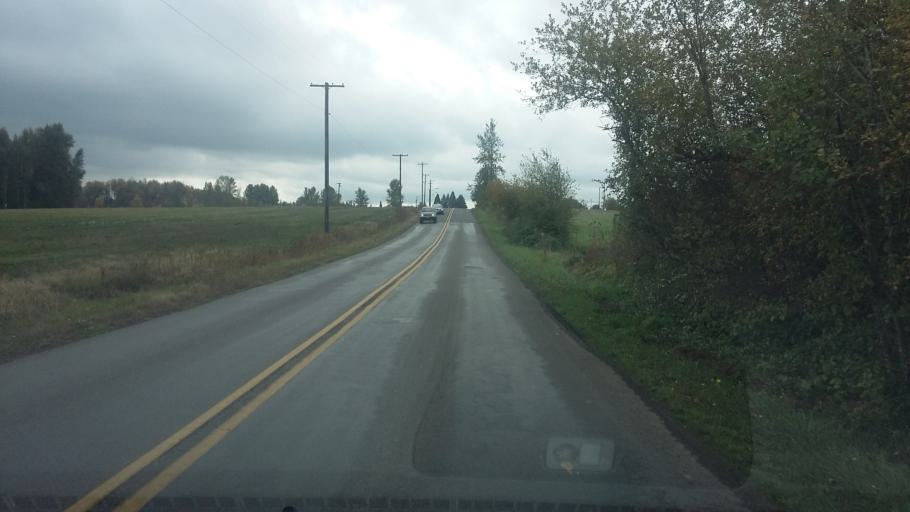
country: US
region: Washington
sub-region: Clark County
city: La Center
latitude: 45.8201
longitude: -122.6825
